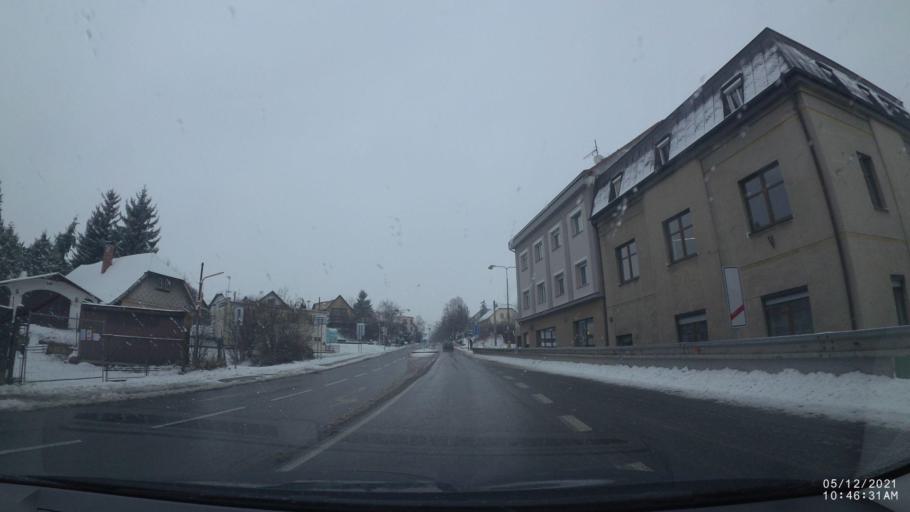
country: CZ
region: Kralovehradecky
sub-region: Okres Rychnov nad Kneznou
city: Rychnov nad Kneznou
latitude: 50.1658
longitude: 16.2713
